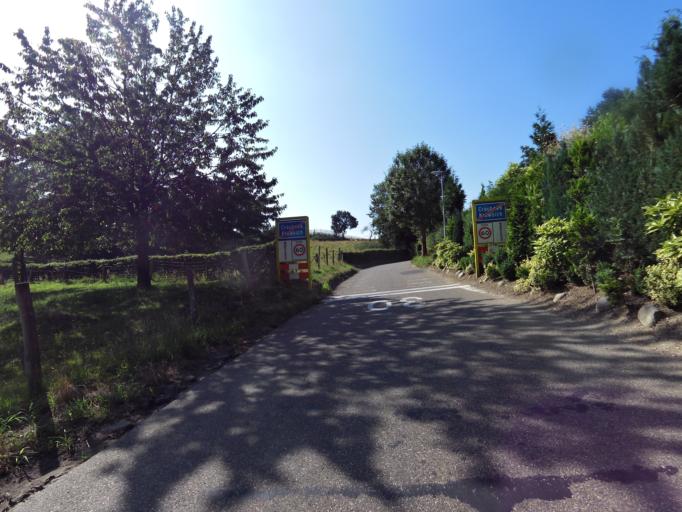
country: NL
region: Limburg
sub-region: Gemeente Voerendaal
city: Klimmen
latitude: 50.8741
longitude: 5.8943
